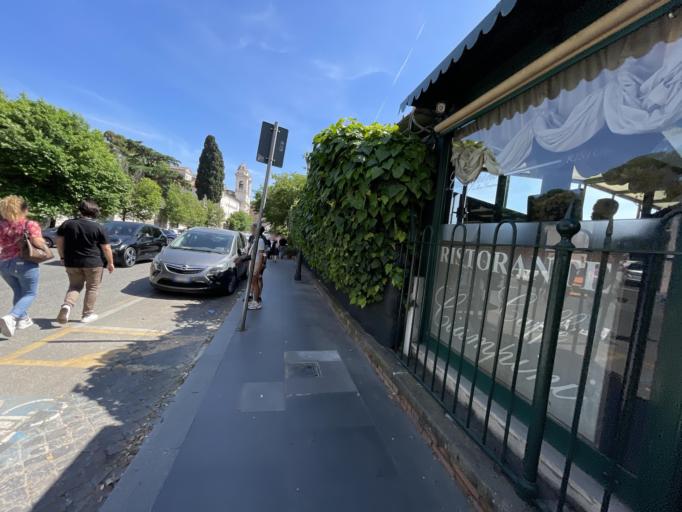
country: VA
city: Vatican City
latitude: 41.9077
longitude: 12.4826
